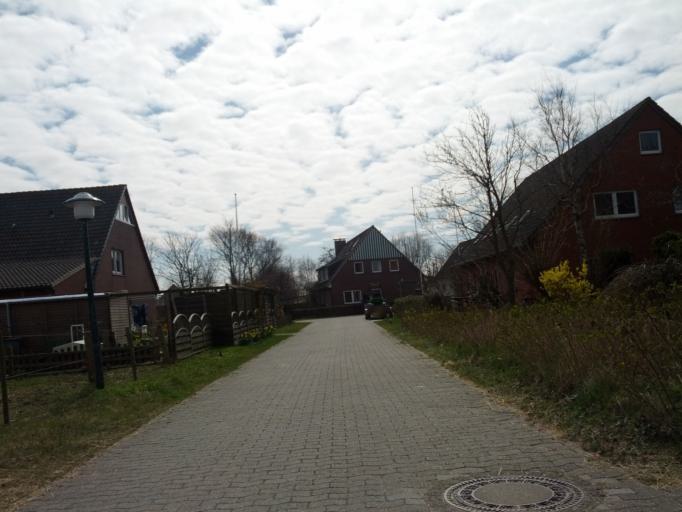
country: DE
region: Lower Saxony
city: Langeoog
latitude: 53.7465
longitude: 7.4913
